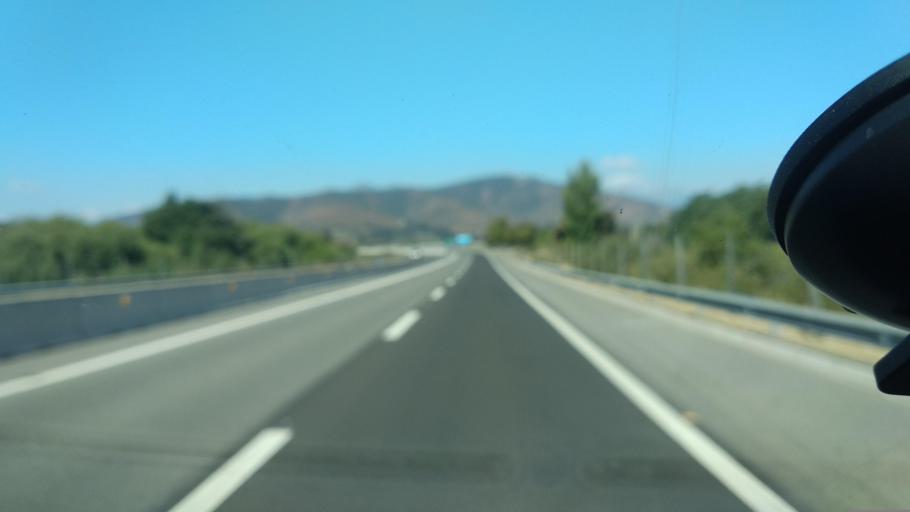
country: CL
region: Valparaiso
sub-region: Provincia de Marga Marga
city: Limache
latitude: -32.9817
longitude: -71.3121
